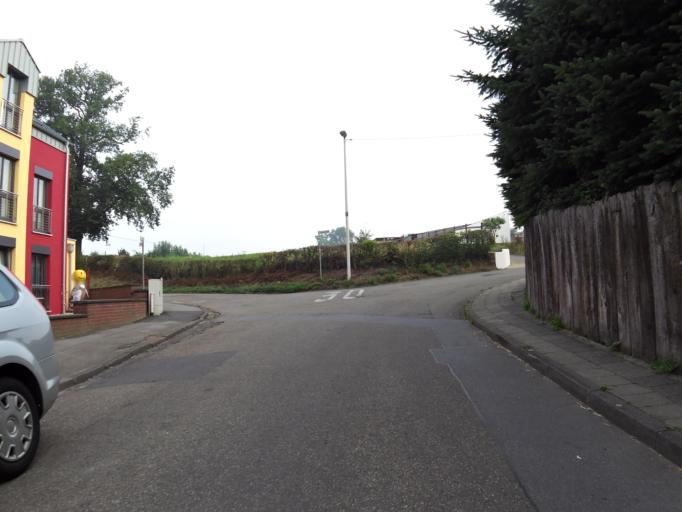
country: DE
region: North Rhine-Westphalia
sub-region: Regierungsbezirk Koln
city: Herzogenrath
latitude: 50.8849
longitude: 6.0985
